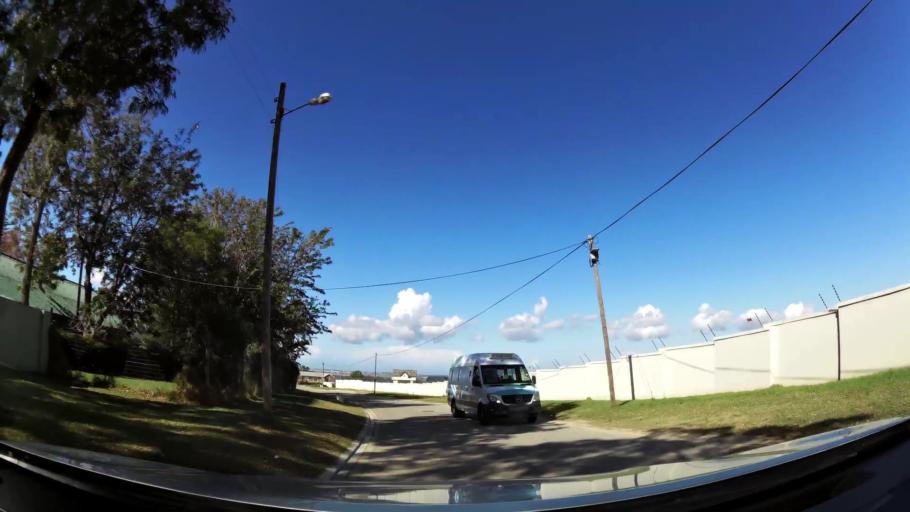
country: ZA
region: Western Cape
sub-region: Eden District Municipality
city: George
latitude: -33.9410
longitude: 22.4058
